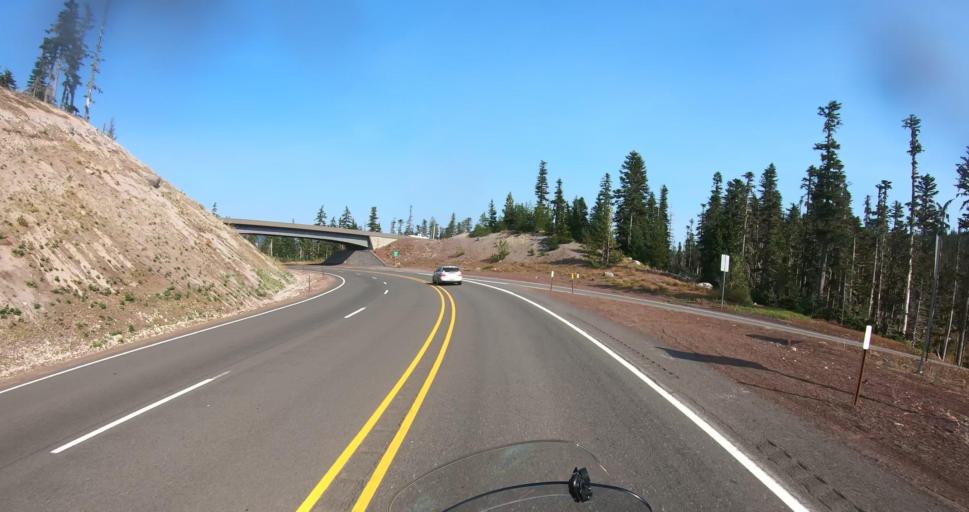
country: US
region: Oregon
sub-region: Hood River County
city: Odell
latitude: 45.3102
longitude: -121.6451
